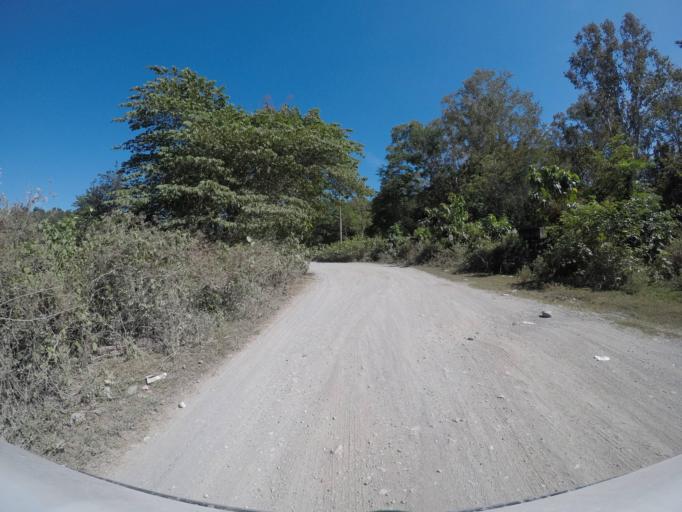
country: TL
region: Manufahi
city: Same
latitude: -8.9595
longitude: 126.0100
